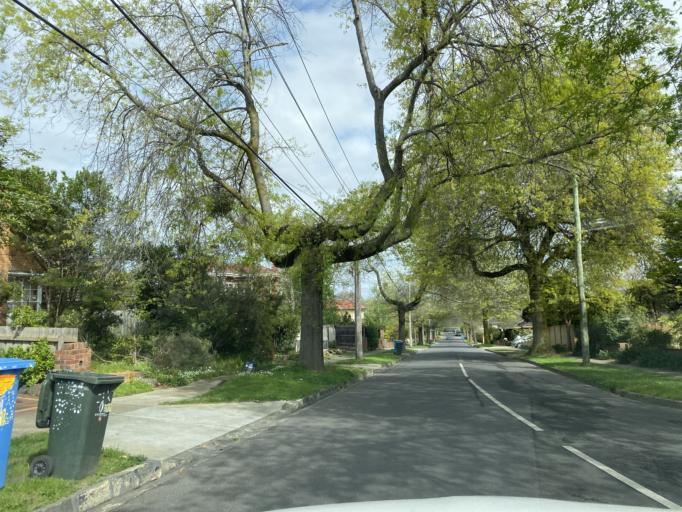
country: AU
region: Victoria
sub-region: Boroondara
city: Ashburton
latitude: -37.8531
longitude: 145.0849
